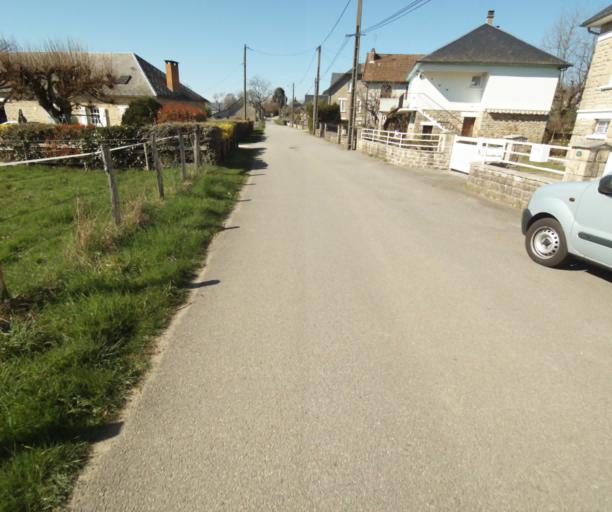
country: FR
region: Limousin
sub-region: Departement de la Correze
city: Chamboulive
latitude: 45.4684
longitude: 1.7373
